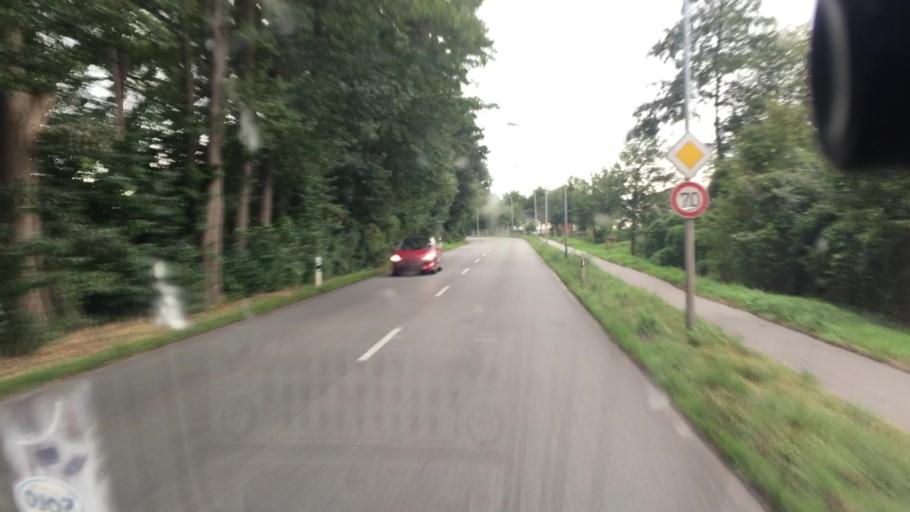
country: DE
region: Lower Saxony
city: Lohne
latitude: 52.6569
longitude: 8.1973
